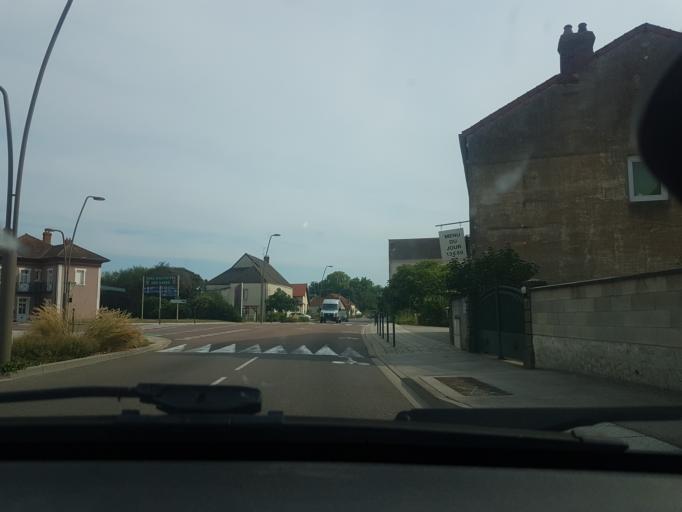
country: FR
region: Bourgogne
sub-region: Departement de Saone-et-Loire
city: Saint-Marcel
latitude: 46.7706
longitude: 4.8935
